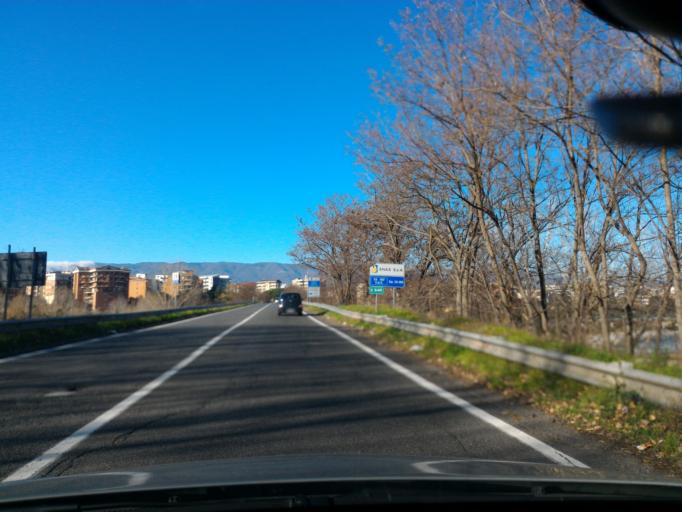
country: IT
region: Calabria
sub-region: Provincia di Cosenza
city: Quattromiglia
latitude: 39.3283
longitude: 16.2519
